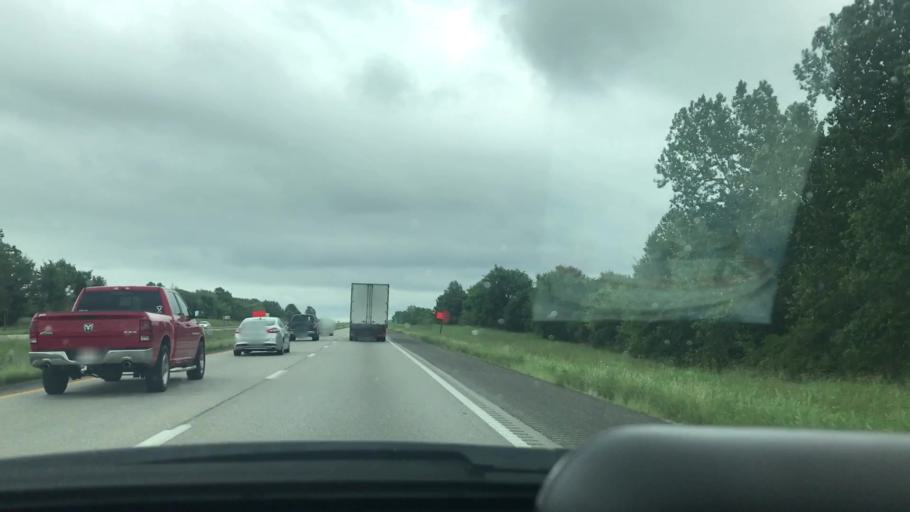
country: US
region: Missouri
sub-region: Christian County
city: Billings
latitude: 37.1862
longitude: -93.6032
